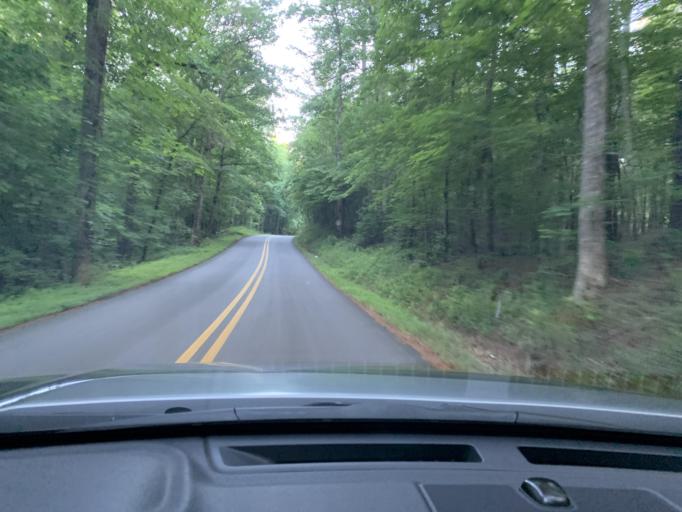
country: US
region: Georgia
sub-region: Bartow County
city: Rydal
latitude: 34.2333
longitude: -84.6627
